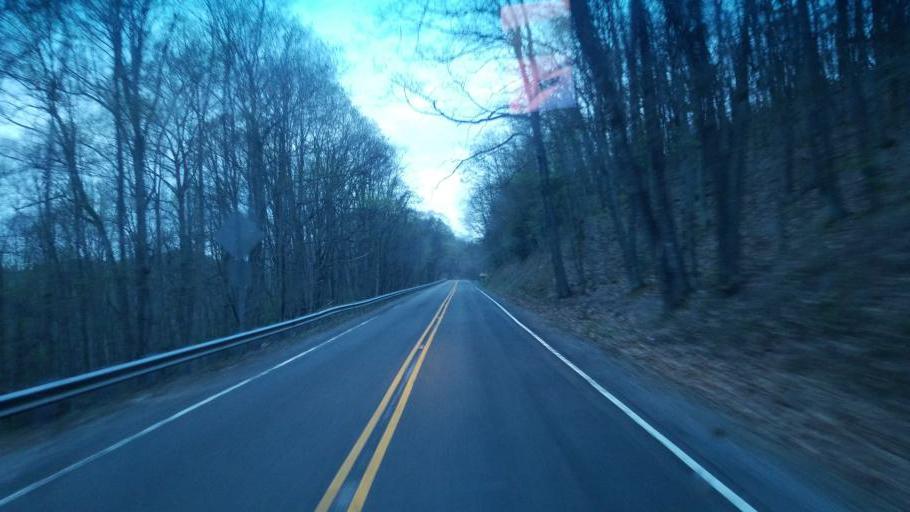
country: US
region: Virginia
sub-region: Smyth County
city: Atkins
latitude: 36.8109
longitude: -81.4250
